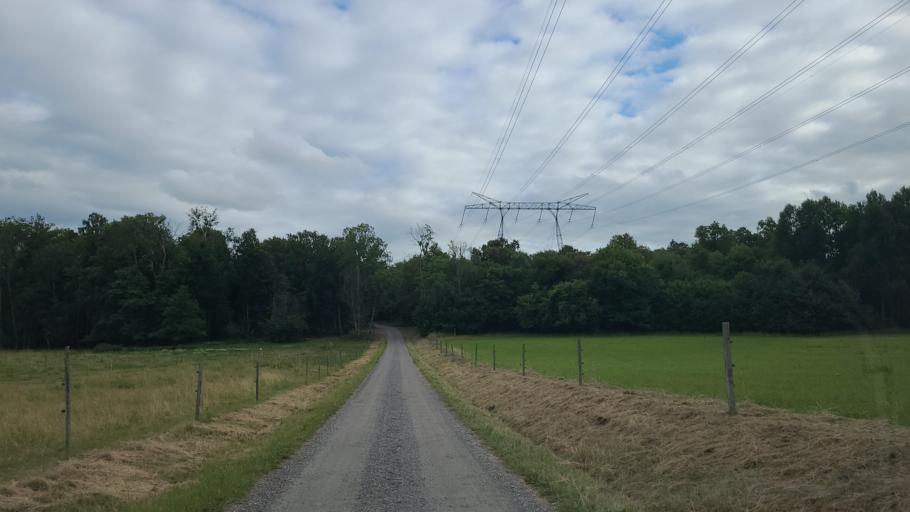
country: SE
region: Stockholm
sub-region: Upplands-Bro Kommun
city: Bro
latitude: 59.4583
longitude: 17.5811
